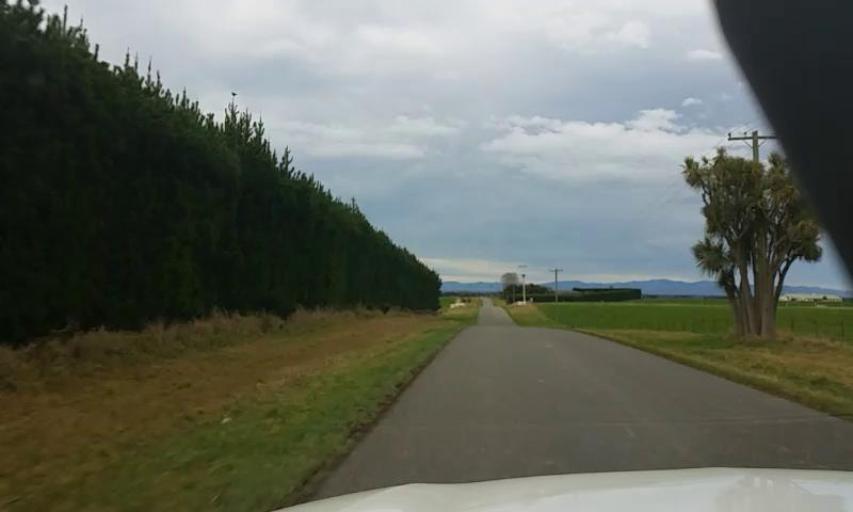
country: NZ
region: Canterbury
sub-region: Waimakariri District
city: Kaiapoi
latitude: -43.2937
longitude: 172.4730
